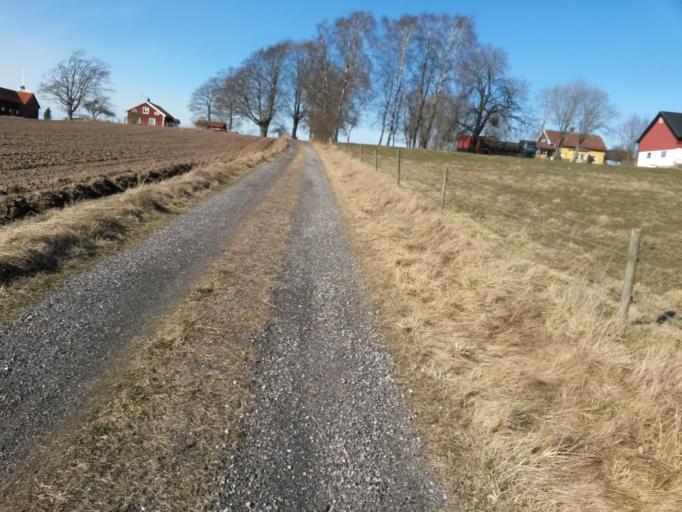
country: SE
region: Vaestra Goetaland
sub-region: Vargarda Kommun
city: Jonstorp
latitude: 57.9783
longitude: 12.6528
